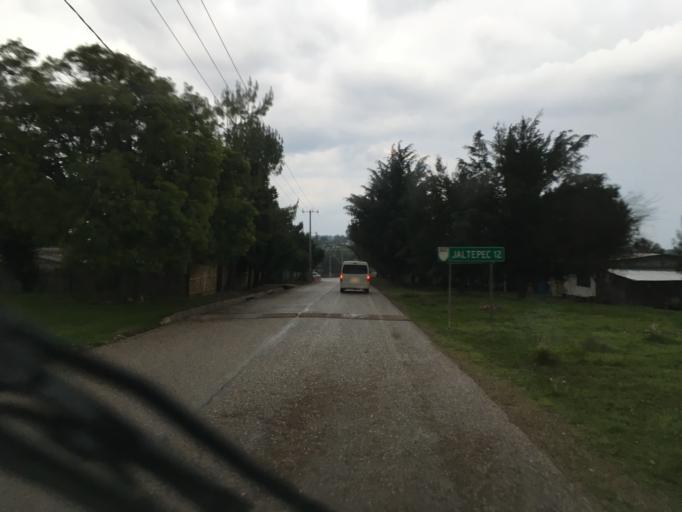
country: MX
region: Oaxaca
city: Santiago Tilantongo
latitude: 17.2881
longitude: -97.2817
